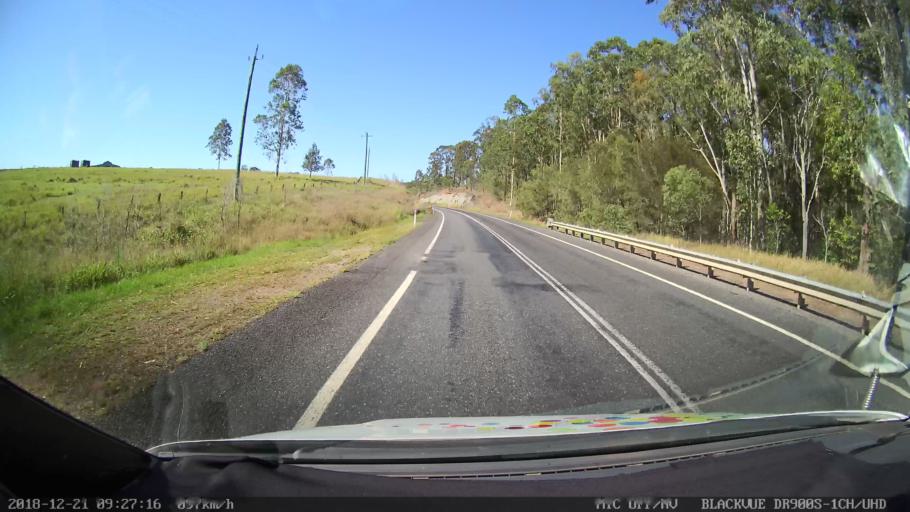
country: AU
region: New South Wales
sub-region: Clarence Valley
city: Maclean
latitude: -29.4005
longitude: 152.9913
